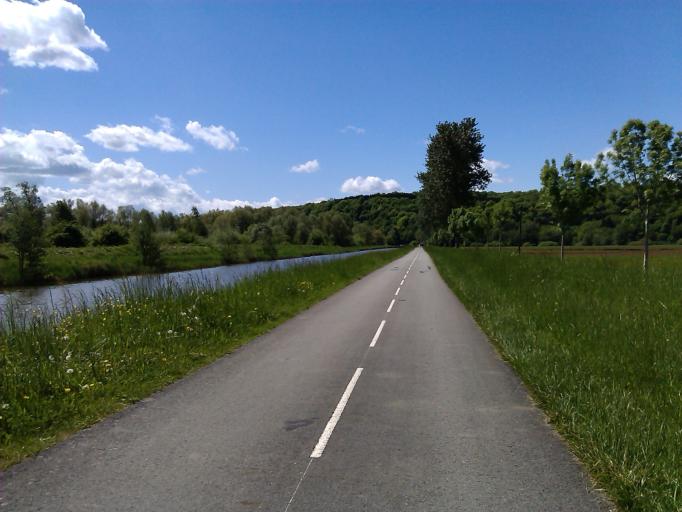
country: FR
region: Franche-Comte
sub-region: Territoire de Belfort
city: Bourogne
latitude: 47.5519
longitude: 6.9149
